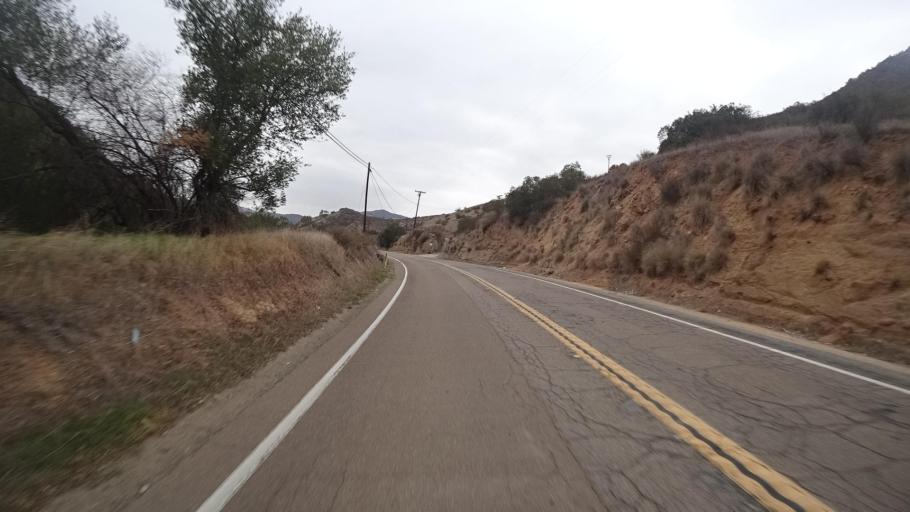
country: US
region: California
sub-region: San Diego County
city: Harbison Canyon
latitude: 32.8122
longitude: -116.8420
